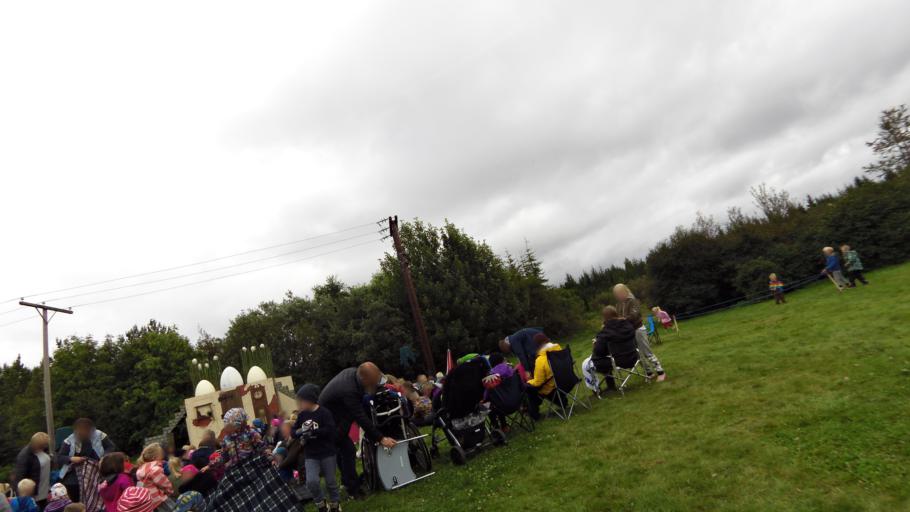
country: IS
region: Capital Region
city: Reykjavik
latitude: 64.1183
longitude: -21.8370
